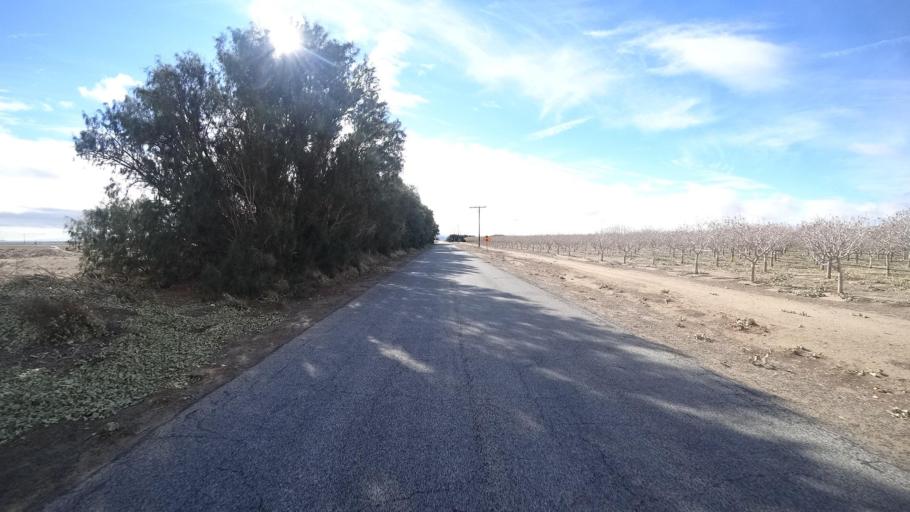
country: US
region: California
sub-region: Kern County
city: Rosamond
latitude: 34.8225
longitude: -118.3086
